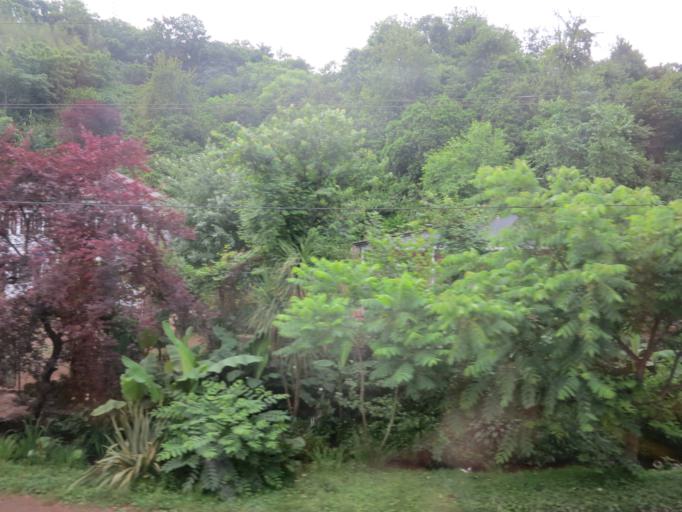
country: GE
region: Ajaria
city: Kobuleti
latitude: 41.7761
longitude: 41.7607
